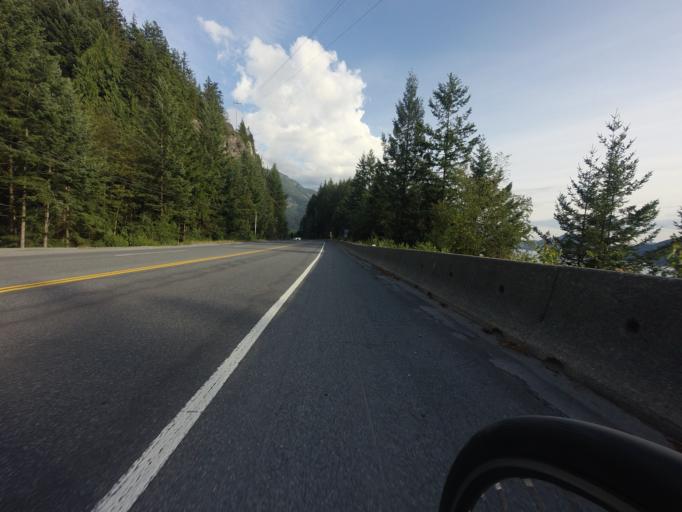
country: CA
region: British Columbia
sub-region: Greater Vancouver Regional District
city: Lions Bay
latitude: 49.6386
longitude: -123.2127
